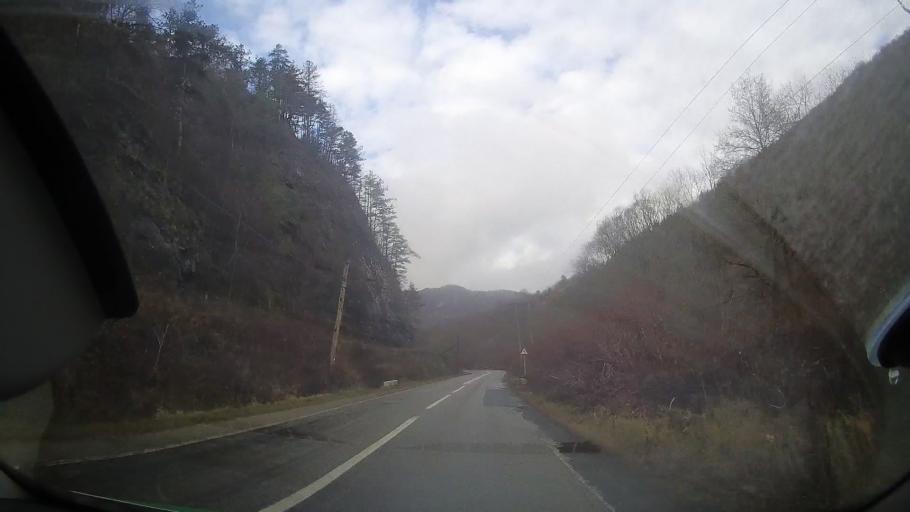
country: RO
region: Alba
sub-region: Comuna Ocolis
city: Ocolis
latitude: 46.4293
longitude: 23.4630
